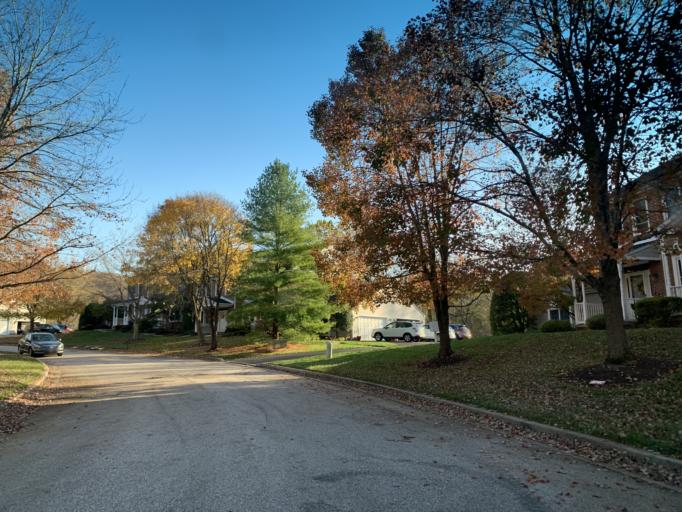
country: US
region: Maryland
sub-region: Baltimore County
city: Hunt Valley
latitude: 39.4941
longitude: -76.6416
